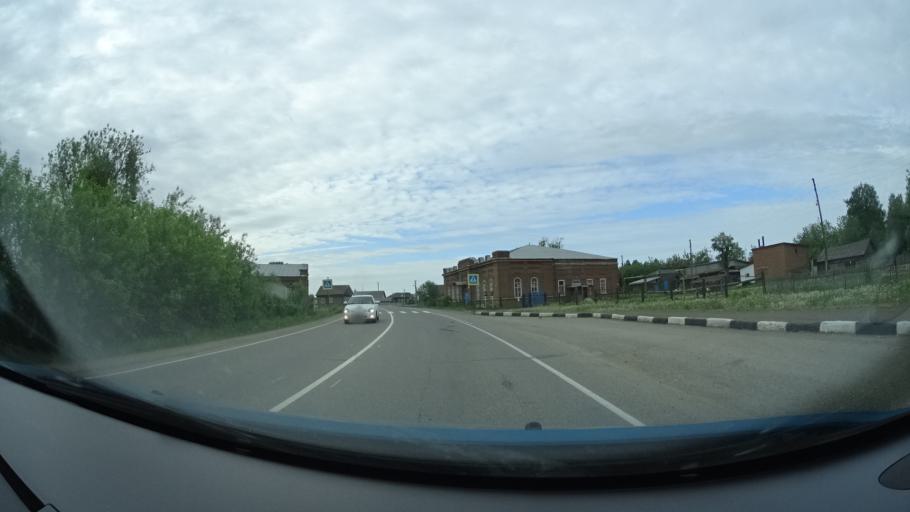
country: RU
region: Perm
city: Barda
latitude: 56.8953
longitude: 55.6020
